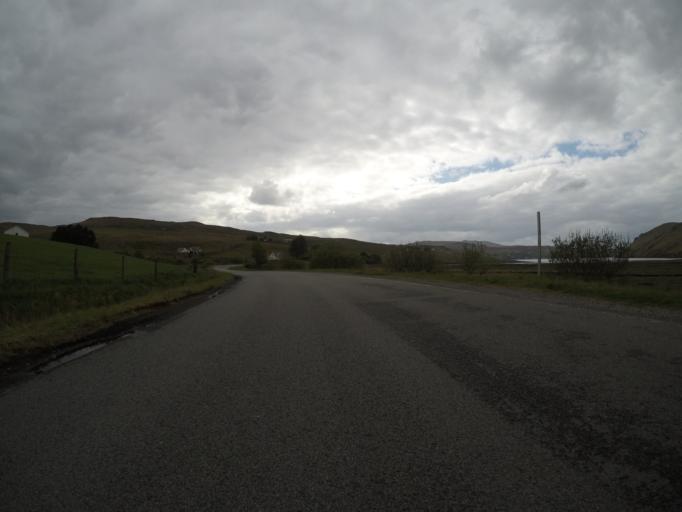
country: GB
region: Scotland
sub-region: Highland
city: Isle of Skye
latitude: 57.2973
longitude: -6.3136
